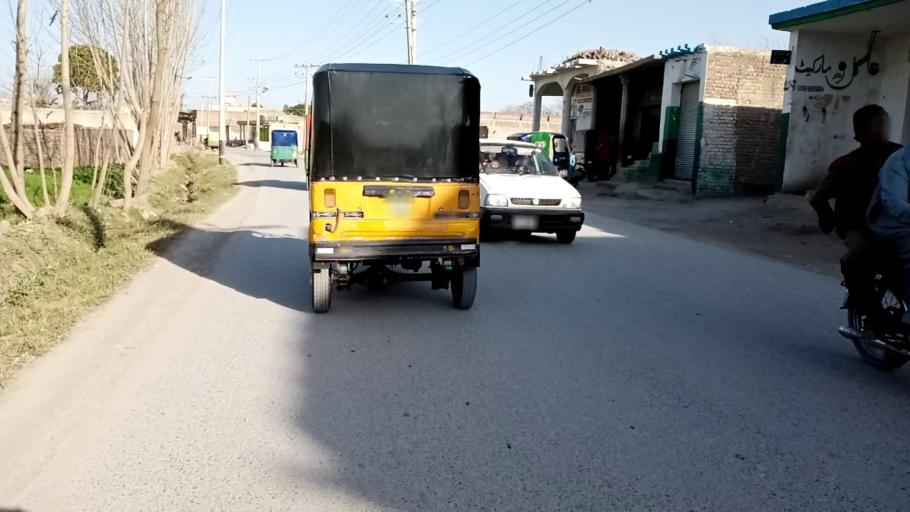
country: PK
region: Khyber Pakhtunkhwa
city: Peshawar
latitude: 34.0553
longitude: 71.5372
